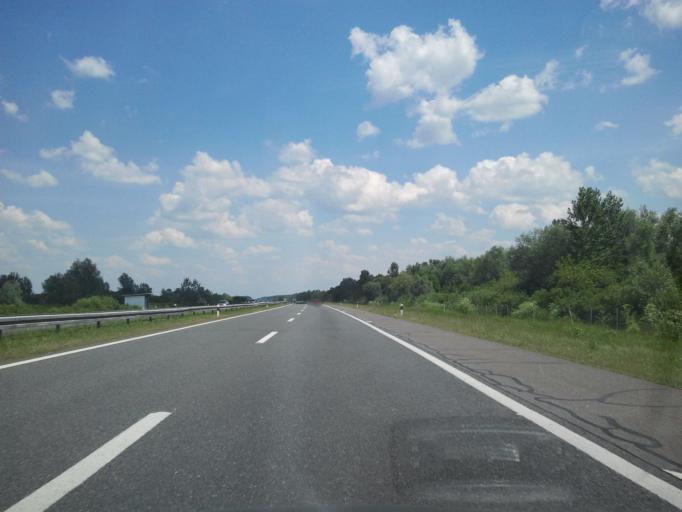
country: HR
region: Brodsko-Posavska
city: Oriovac
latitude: 45.1507
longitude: 17.7771
